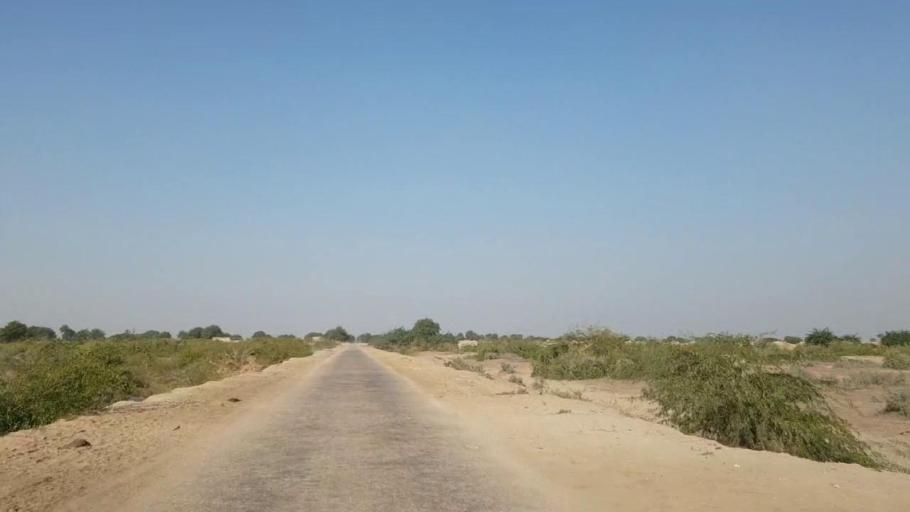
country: PK
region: Sindh
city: Digri
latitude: 25.0021
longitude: 69.1065
